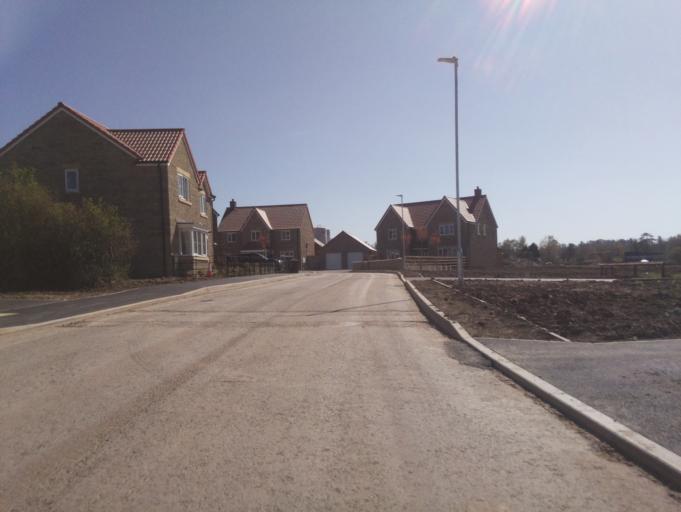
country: GB
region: England
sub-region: South Gloucestershire
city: Falfield
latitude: 51.6401
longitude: -2.4613
